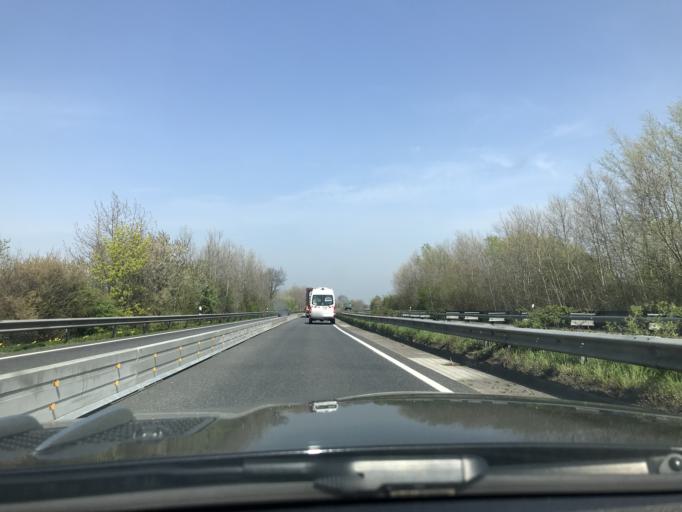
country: DE
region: Schleswig-Holstein
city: Neustadt in Holstein
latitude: 54.1161
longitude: 10.7863
